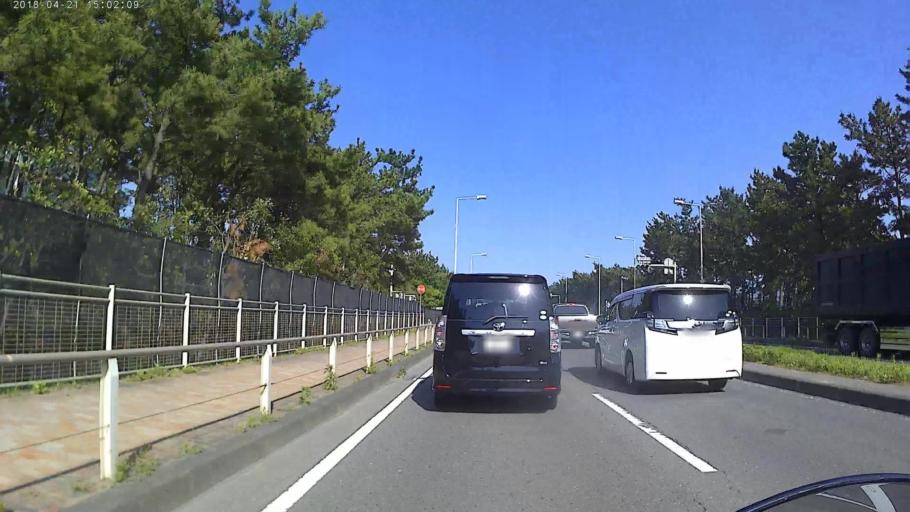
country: JP
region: Kanagawa
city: Chigasaki
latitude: 35.3188
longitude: 139.4073
